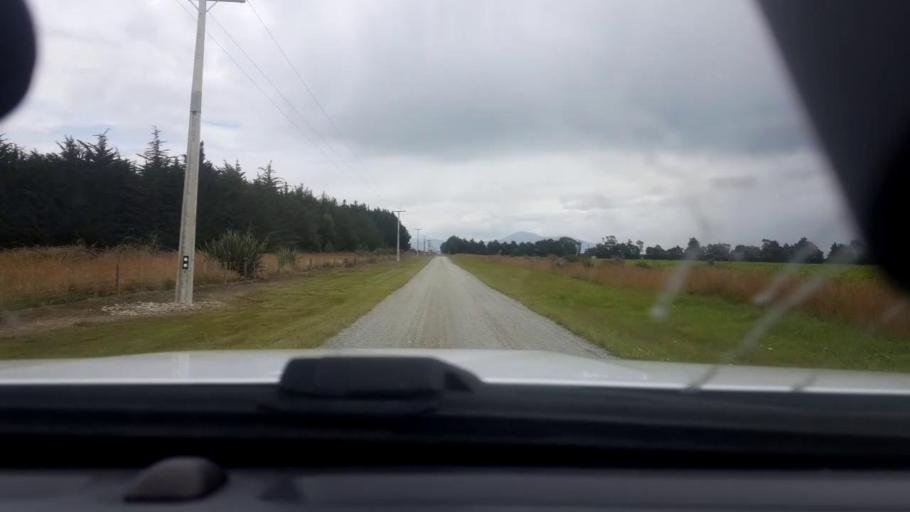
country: NZ
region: Canterbury
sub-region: Timaru District
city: Timaru
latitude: -44.1622
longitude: 171.4061
